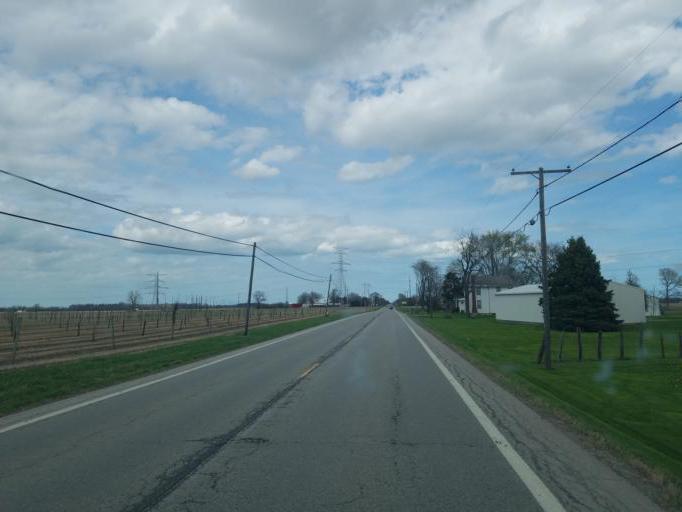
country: US
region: Ohio
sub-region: Erie County
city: Sandusky
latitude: 41.3802
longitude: -82.7403
